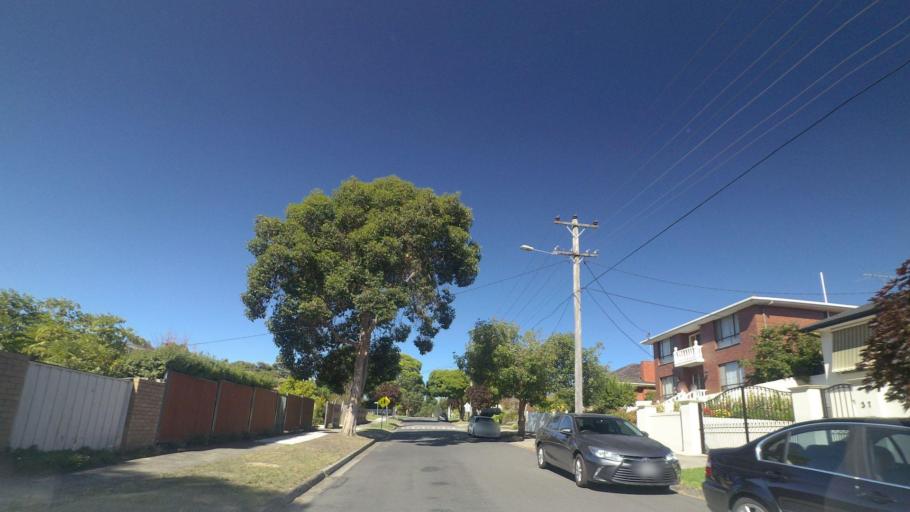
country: AU
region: Victoria
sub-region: Manningham
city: Donvale
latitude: -37.7867
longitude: 145.1678
